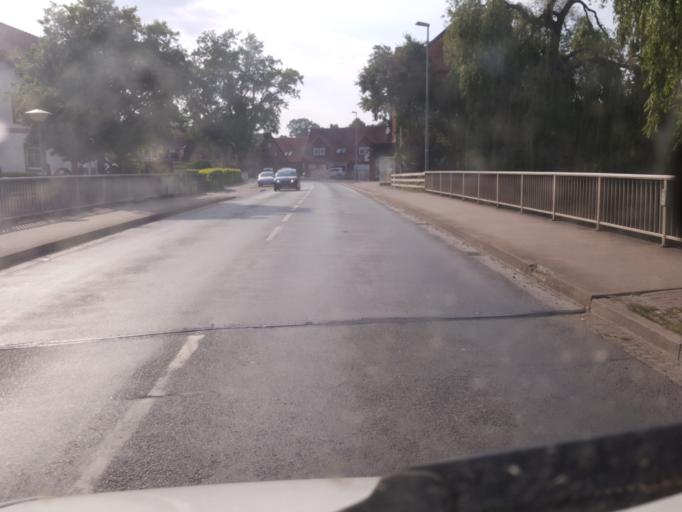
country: DE
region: Lower Saxony
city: Liebenau
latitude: 52.6042
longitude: 9.0949
